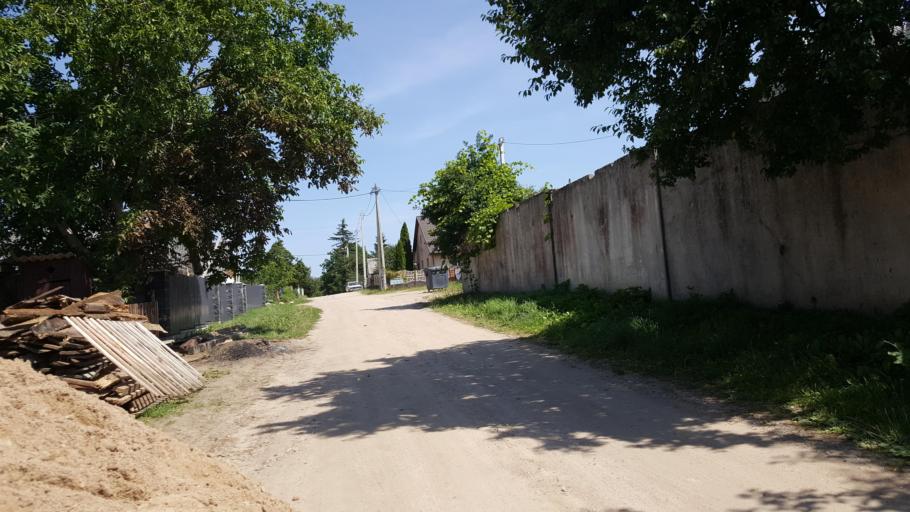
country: BY
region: Brest
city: Vysokaye
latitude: 52.3618
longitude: 23.3808
